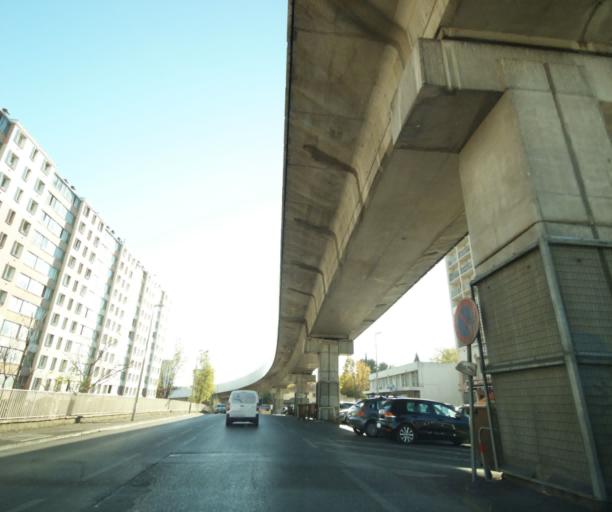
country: FR
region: Provence-Alpes-Cote d'Azur
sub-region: Departement des Bouches-du-Rhone
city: Marseille 13
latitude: 43.3314
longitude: 5.4283
